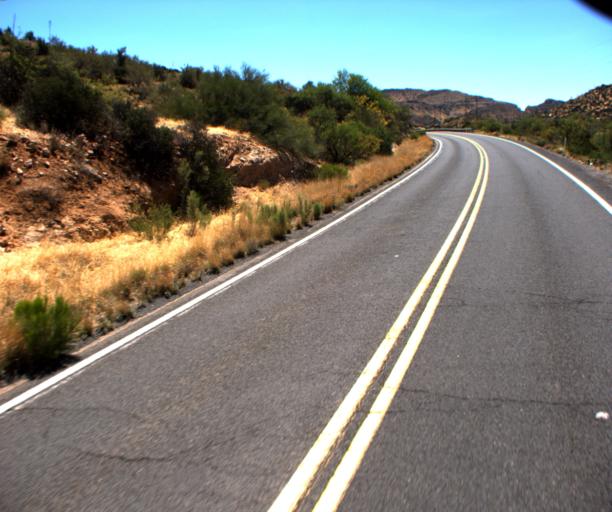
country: US
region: Arizona
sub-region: Pinal County
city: Superior
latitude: 33.2225
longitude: -111.0755
